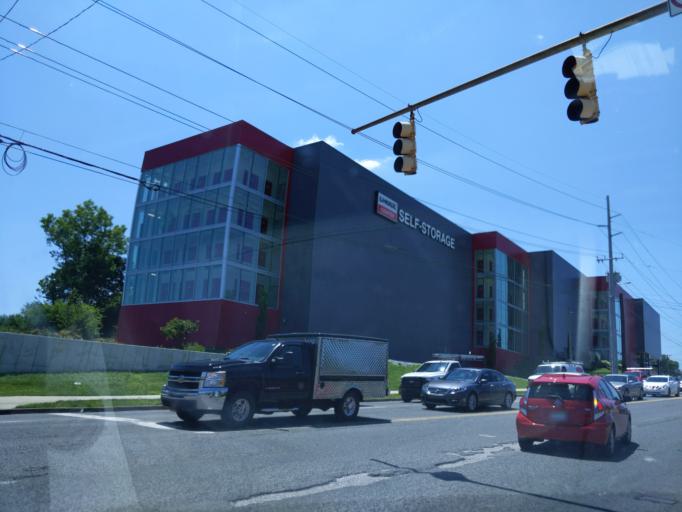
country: US
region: Tennessee
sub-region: Davidson County
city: Nashville
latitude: 36.1467
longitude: -86.7438
